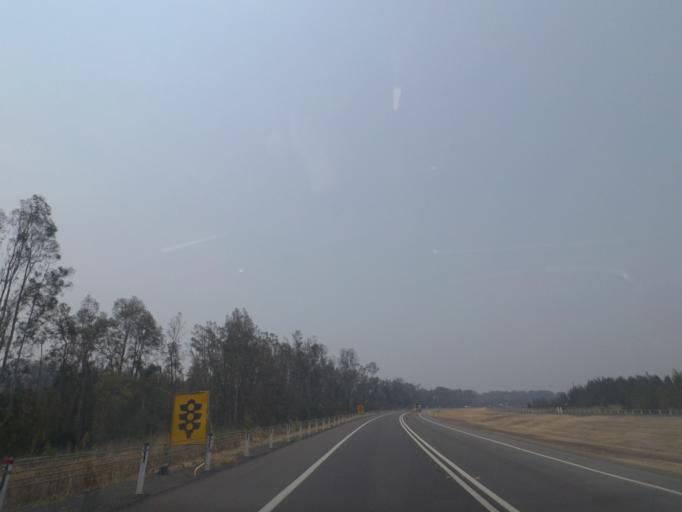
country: AU
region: New South Wales
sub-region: Ballina
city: Ballina
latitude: -28.8697
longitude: 153.4917
